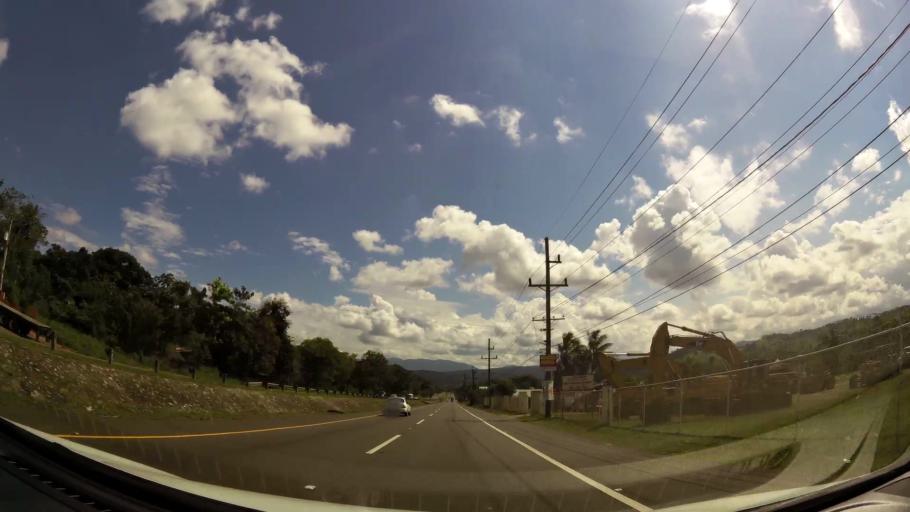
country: DO
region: La Vega
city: Rio Verde Arriba
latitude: 19.2735
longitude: -70.5702
